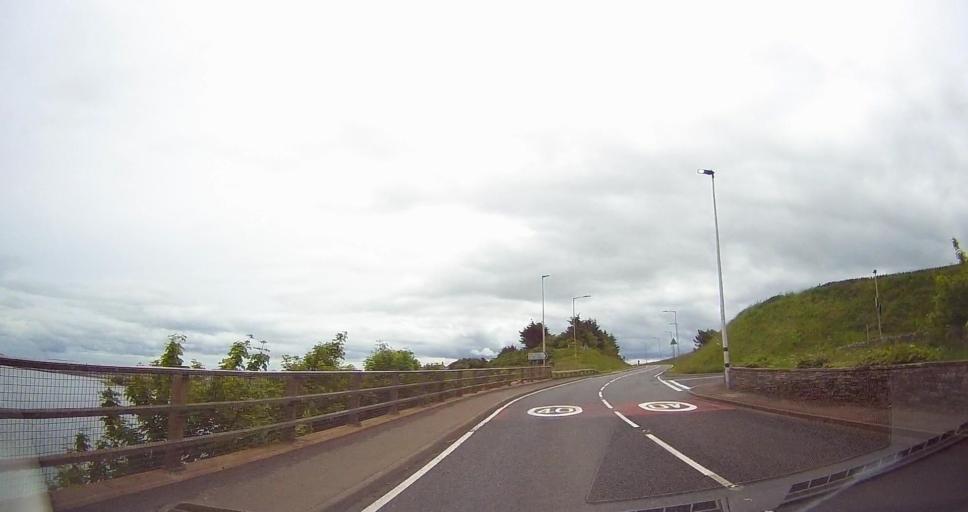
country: GB
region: Scotland
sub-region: Highland
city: Thurso
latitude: 58.6067
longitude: -3.5512
